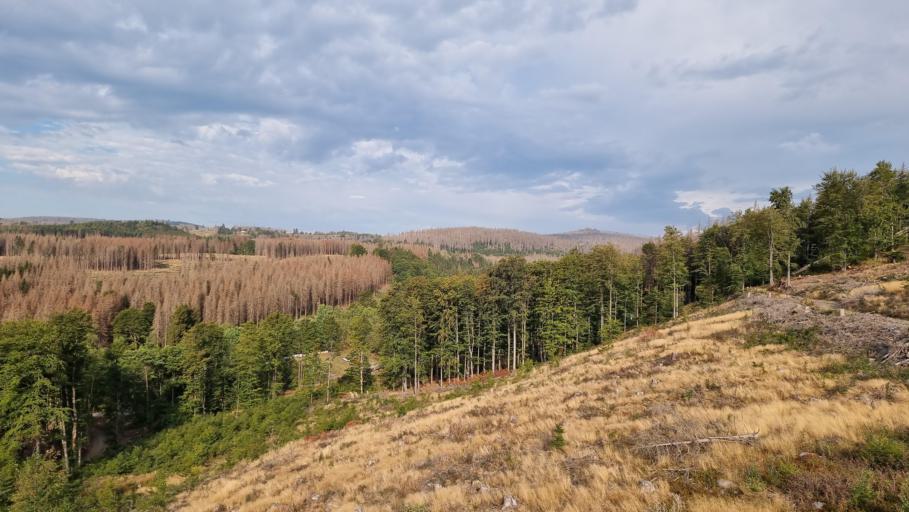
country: DE
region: Lower Saxony
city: Braunlage
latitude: 51.7389
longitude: 10.6154
